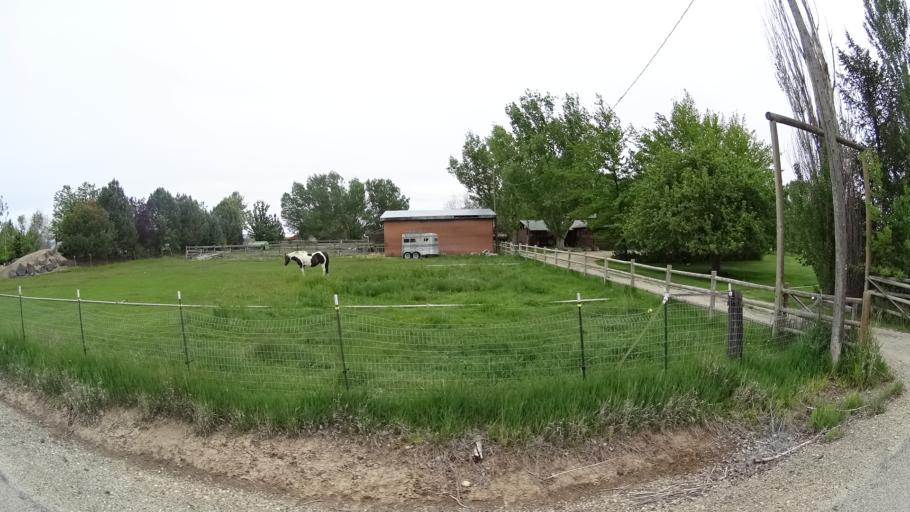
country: US
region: Idaho
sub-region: Ada County
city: Kuna
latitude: 43.4951
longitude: -116.3395
